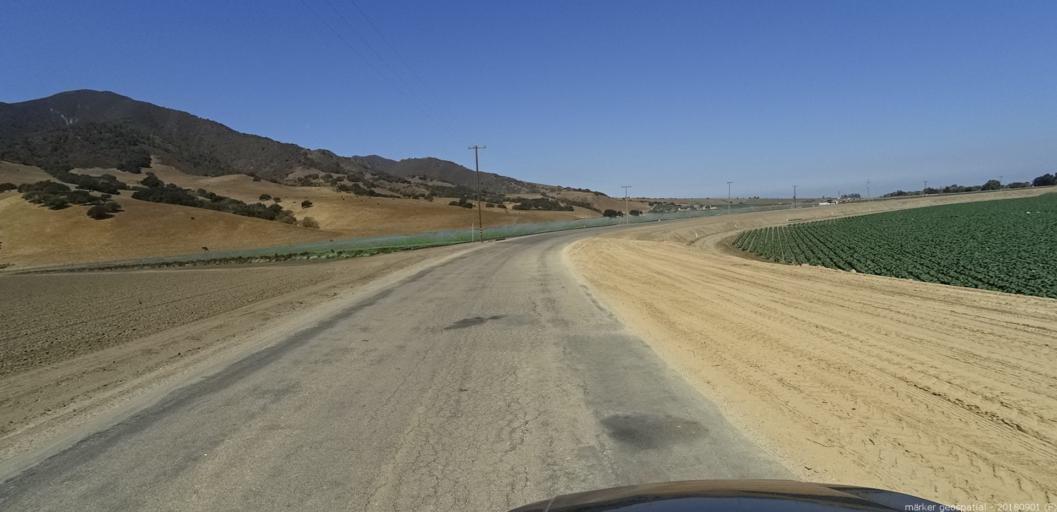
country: US
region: California
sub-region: Monterey County
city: Chualar
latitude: 36.5343
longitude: -121.5404
